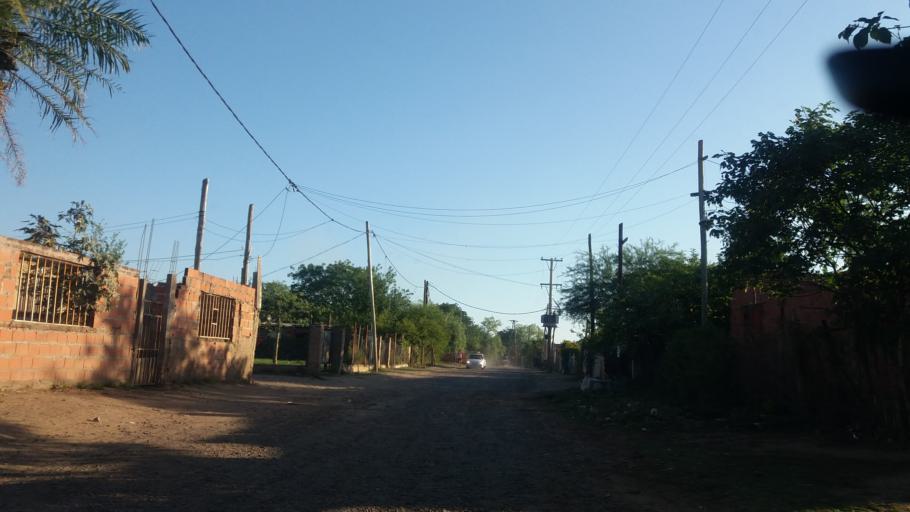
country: AR
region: Corrientes
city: Corrientes
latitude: -27.5164
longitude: -58.8295
